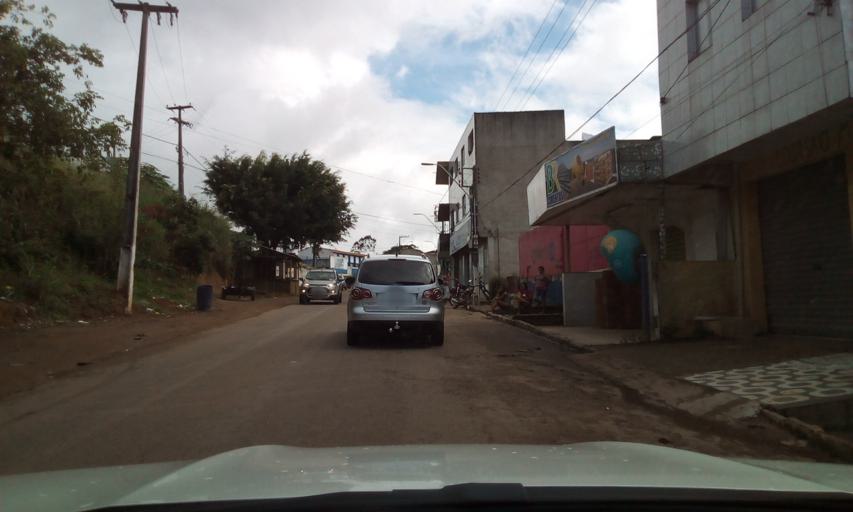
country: BR
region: Paraiba
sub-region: Areia
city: Areia
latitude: -6.9712
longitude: -35.6929
